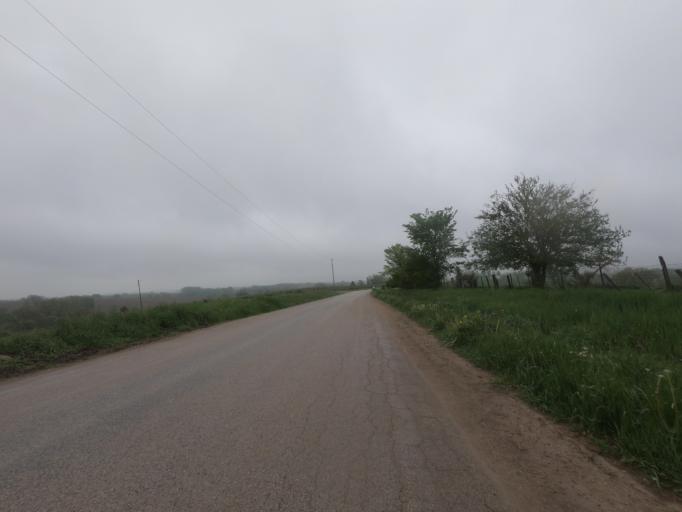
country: US
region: Wisconsin
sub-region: Grant County
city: Hazel Green
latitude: 42.4971
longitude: -90.5020
